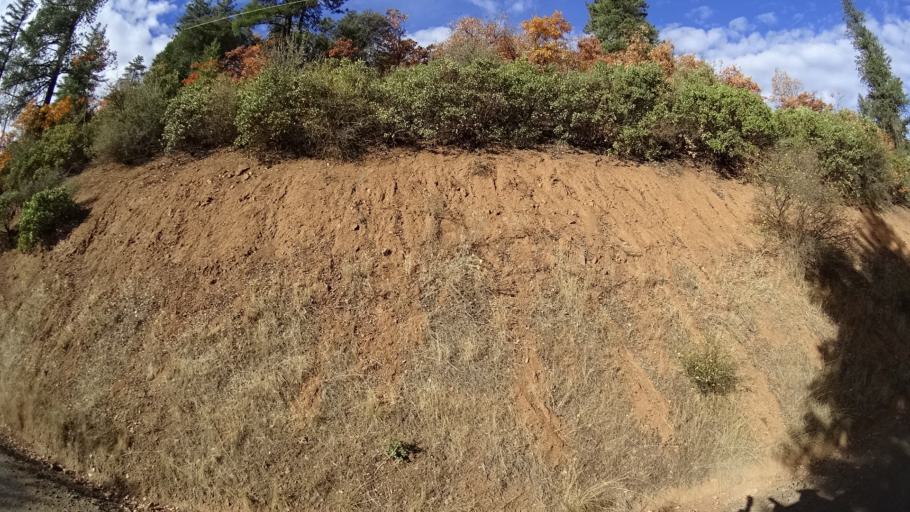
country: US
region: California
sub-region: Siskiyou County
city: Yreka
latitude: 41.7062
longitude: -122.8156
